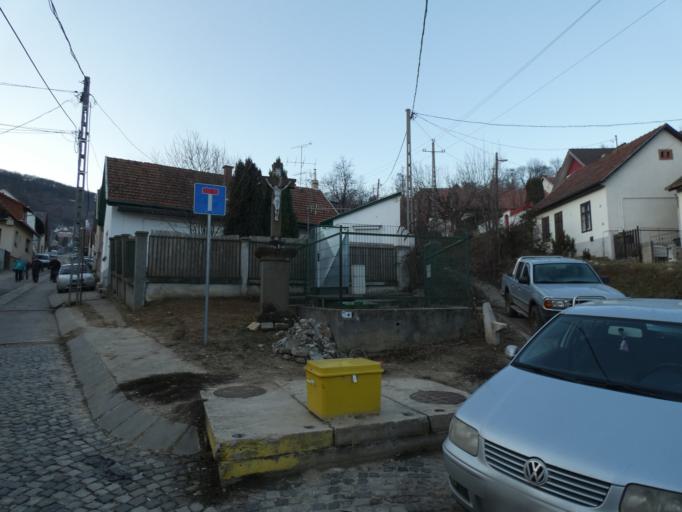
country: HU
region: Pest
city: Nagymaros
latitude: 47.7924
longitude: 18.9540
